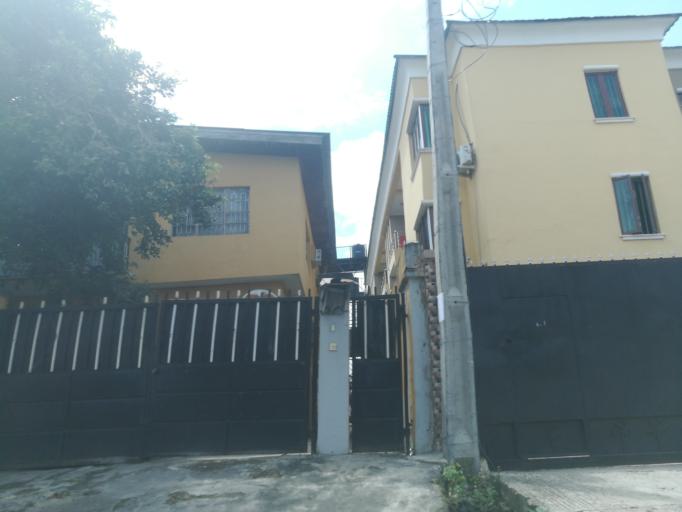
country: NG
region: Lagos
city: Somolu
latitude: 6.5266
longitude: 3.3823
